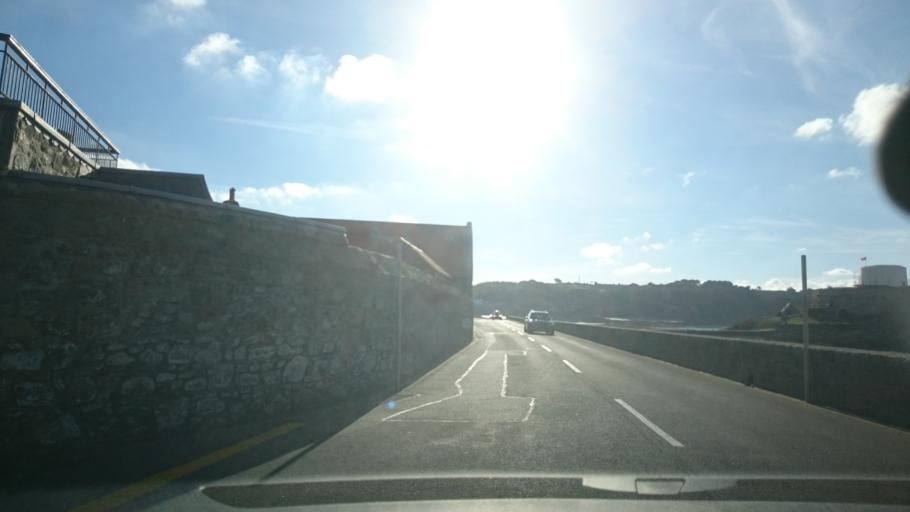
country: GG
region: St Peter Port
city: Saint Peter Port
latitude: 49.4398
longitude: -2.6521
